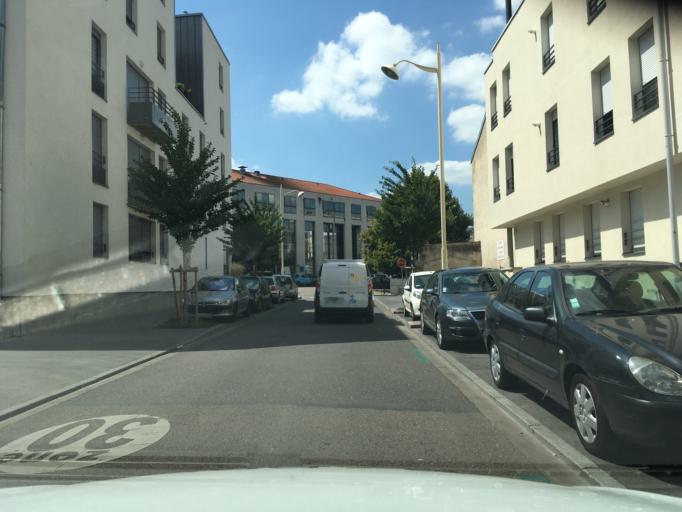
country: FR
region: Lorraine
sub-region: Departement de Meurthe-et-Moselle
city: Nancy
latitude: 48.6862
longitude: 6.1889
